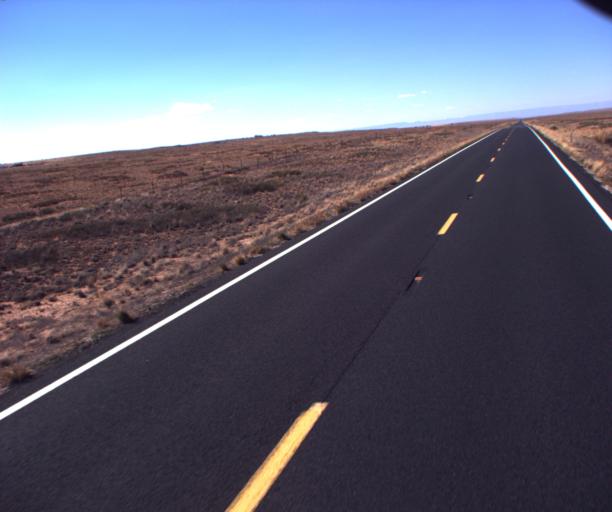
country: US
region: Arizona
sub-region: Coconino County
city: Tuba City
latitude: 36.0135
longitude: -111.0838
